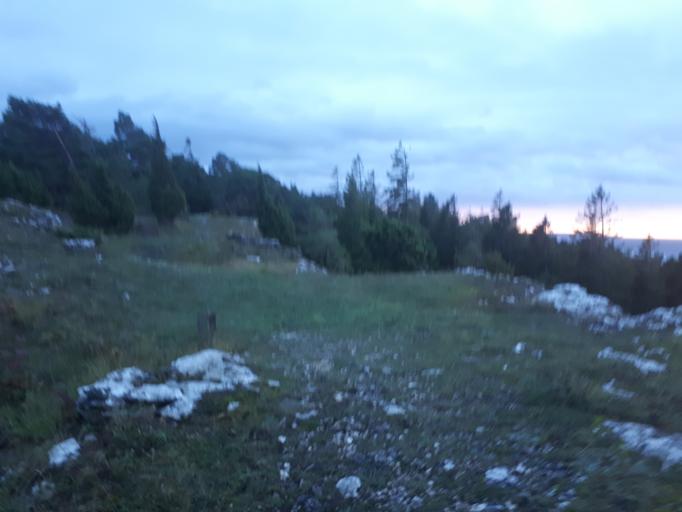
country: SE
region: Gotland
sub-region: Gotland
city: Visby
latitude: 57.6846
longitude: 18.3476
